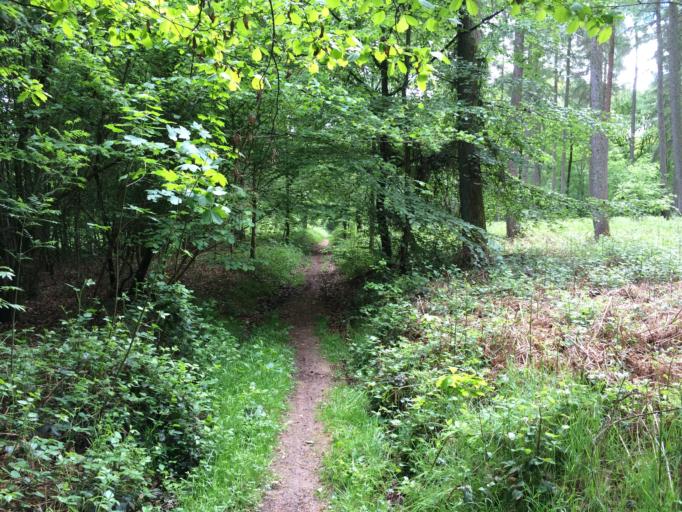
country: BE
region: Wallonia
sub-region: Province de Namur
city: Yvoir
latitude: 50.3395
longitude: 4.9493
